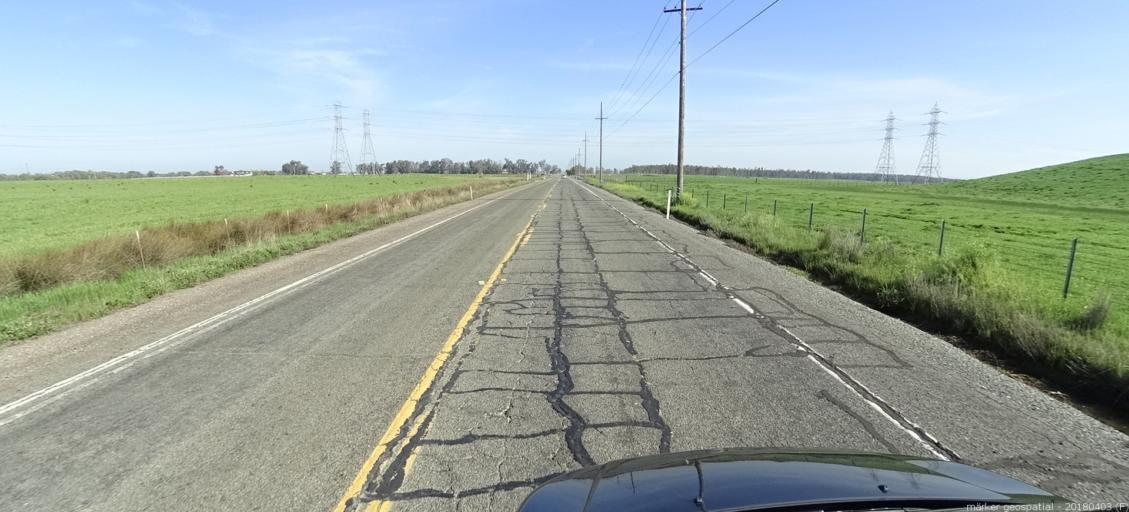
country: US
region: California
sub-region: Sacramento County
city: Clay
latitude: 38.3446
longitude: -121.1684
